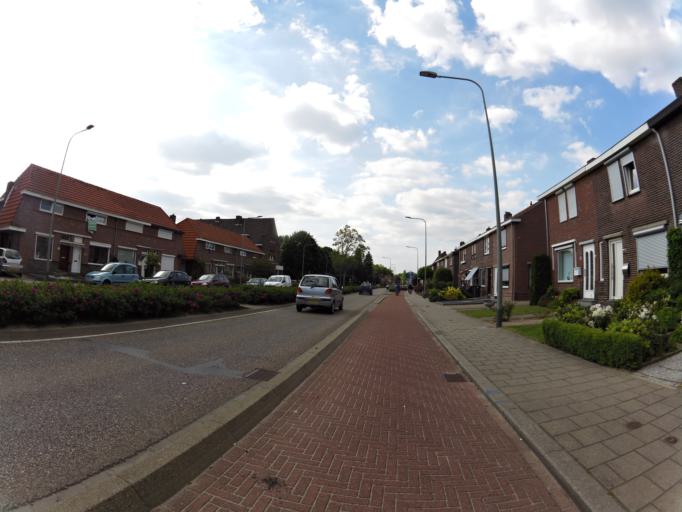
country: NL
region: Limburg
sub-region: Gemeente Brunssum
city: Brunssum
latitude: 50.9345
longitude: 5.9741
